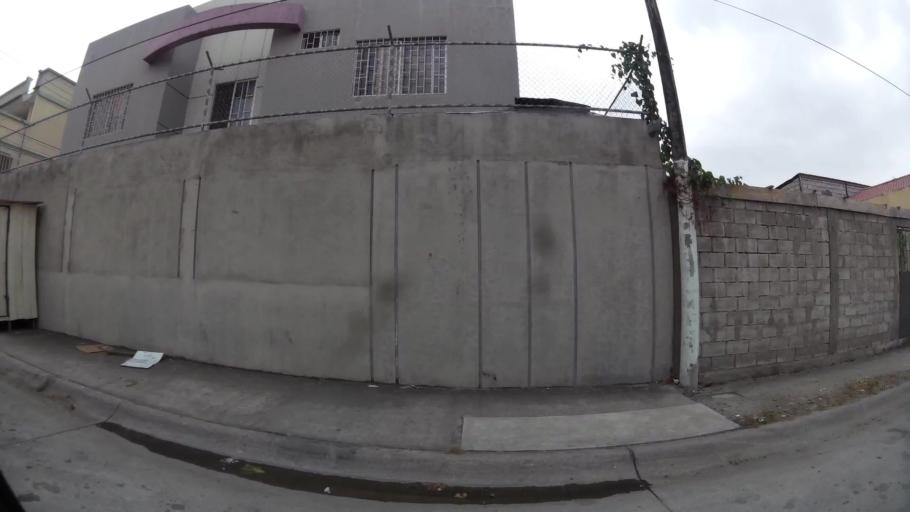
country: EC
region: Guayas
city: Eloy Alfaro
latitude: -2.1330
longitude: -79.8828
